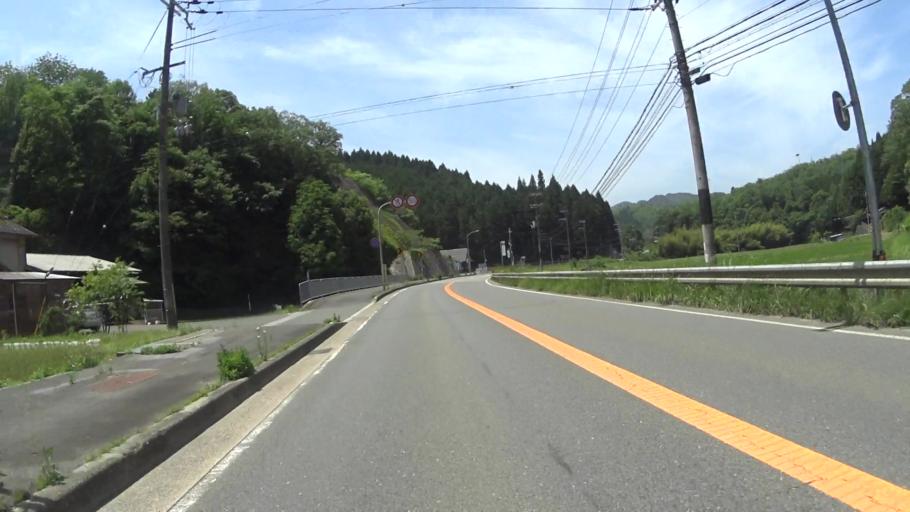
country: JP
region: Kyoto
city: Ayabe
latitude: 35.1852
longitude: 135.3396
